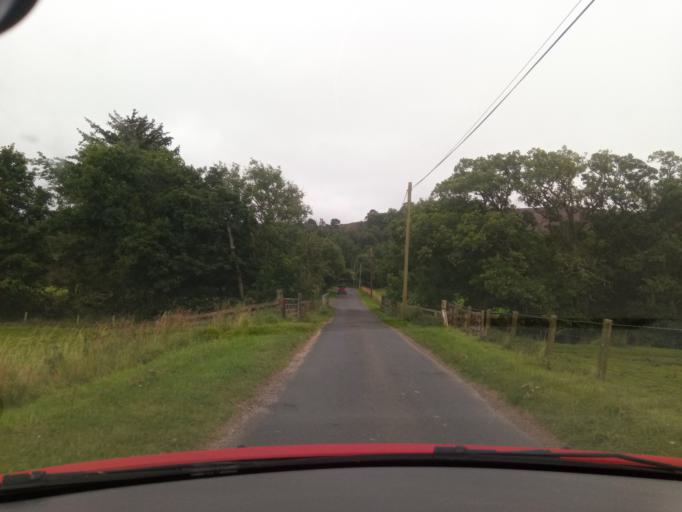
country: GB
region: England
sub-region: Northumberland
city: Rothbury
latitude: 55.2918
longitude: -2.0436
